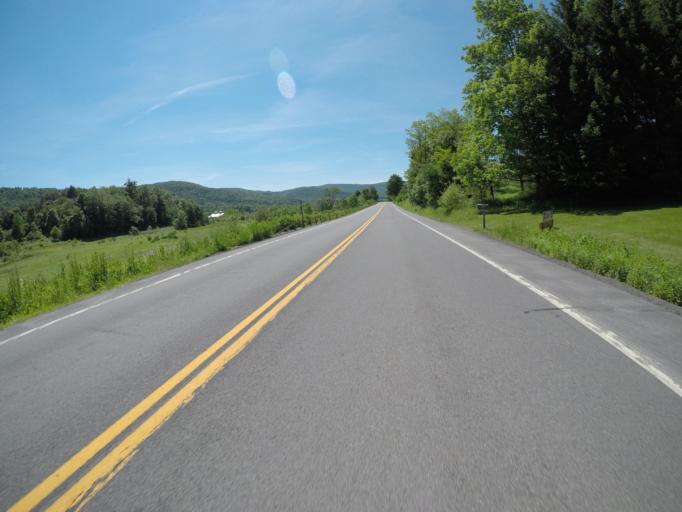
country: US
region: New York
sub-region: Delaware County
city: Delhi
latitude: 42.2291
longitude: -74.9708
